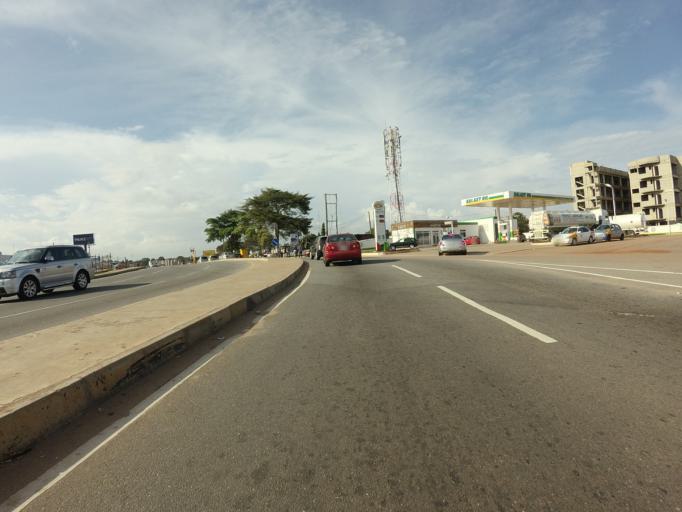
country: GH
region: Greater Accra
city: Medina Estates
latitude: 5.6251
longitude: -0.1527
